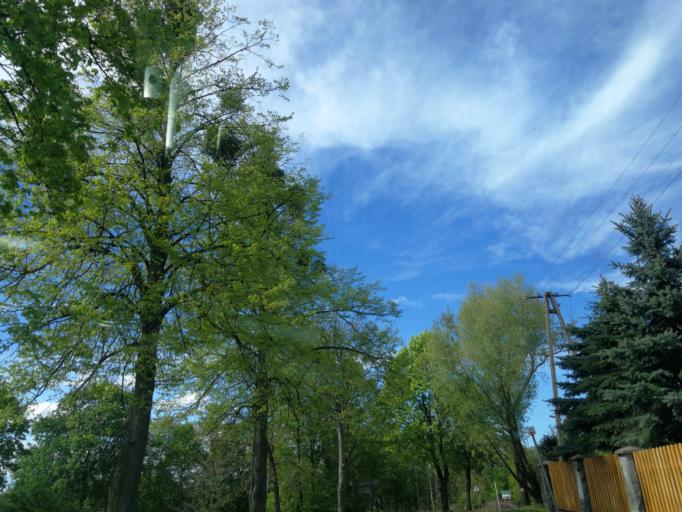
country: PL
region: Warmian-Masurian Voivodeship
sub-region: Powiat ilawski
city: Ilawa
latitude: 53.6319
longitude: 19.6605
